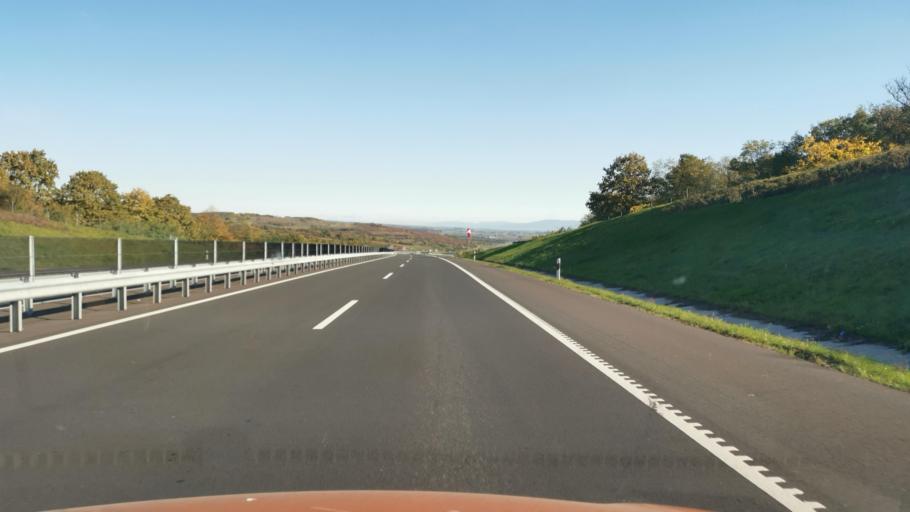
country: HU
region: Borsod-Abauj-Zemplen
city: Szikszo
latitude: 48.2200
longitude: 20.9367
